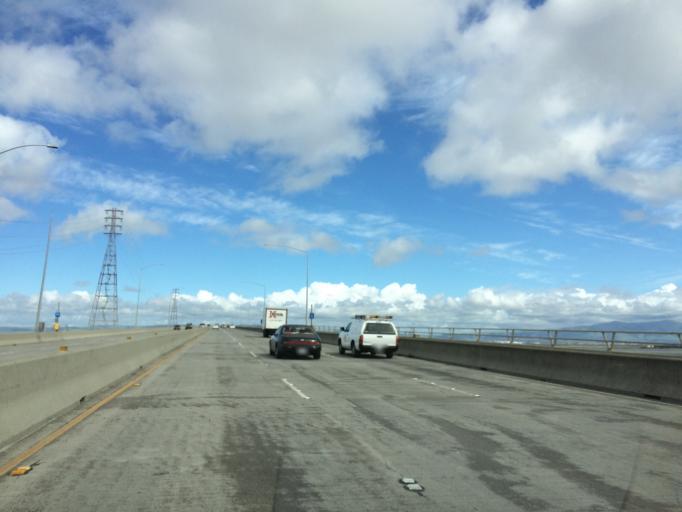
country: US
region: California
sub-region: San Mateo County
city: East Palo Alto
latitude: 37.5003
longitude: -122.1271
